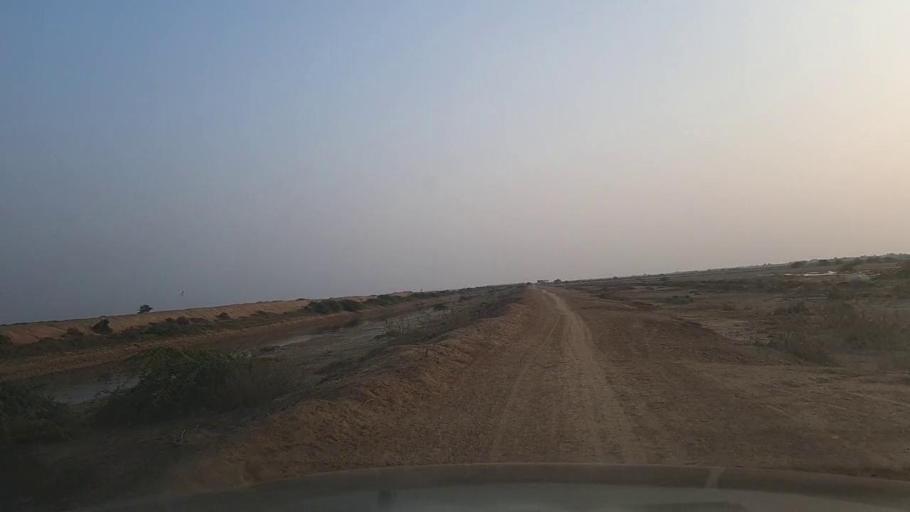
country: PK
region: Sindh
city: Jati
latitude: 24.5361
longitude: 68.4085
